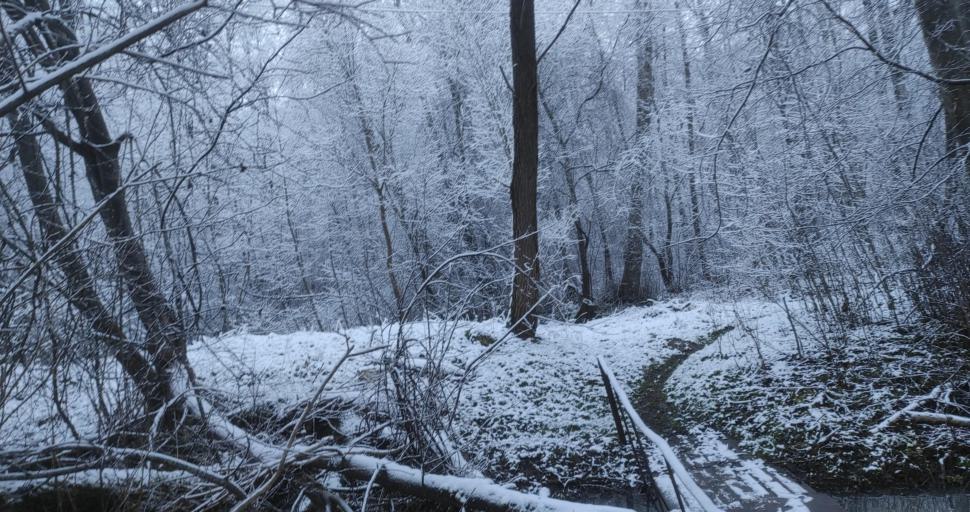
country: LV
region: Skrunda
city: Skrunda
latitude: 56.8742
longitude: 22.2275
